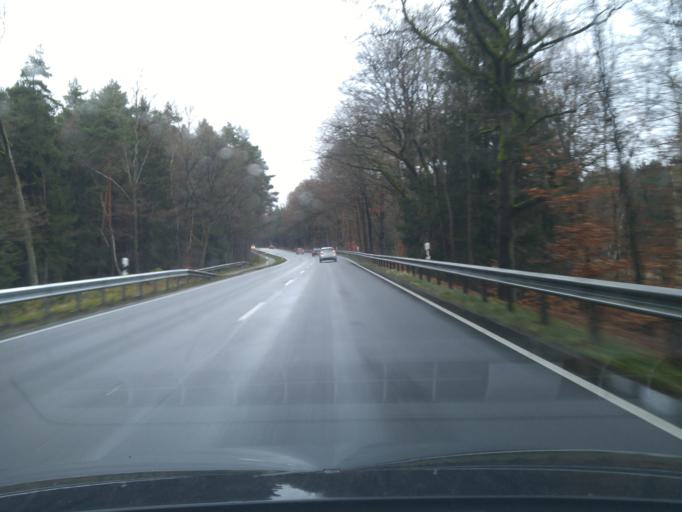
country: DE
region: Lower Saxony
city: Suderburg
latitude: 52.8781
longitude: 10.4994
